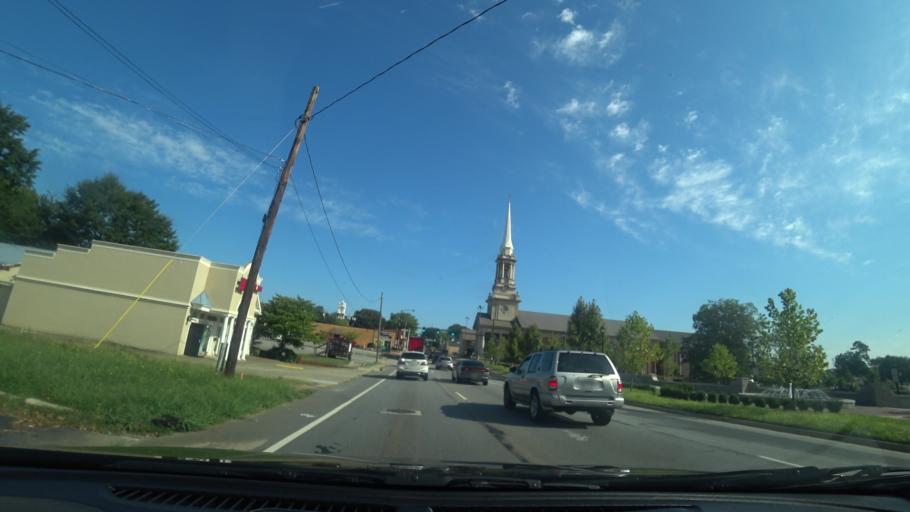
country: US
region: Georgia
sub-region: Gwinnett County
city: Lawrenceville
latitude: 33.9543
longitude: -83.9882
